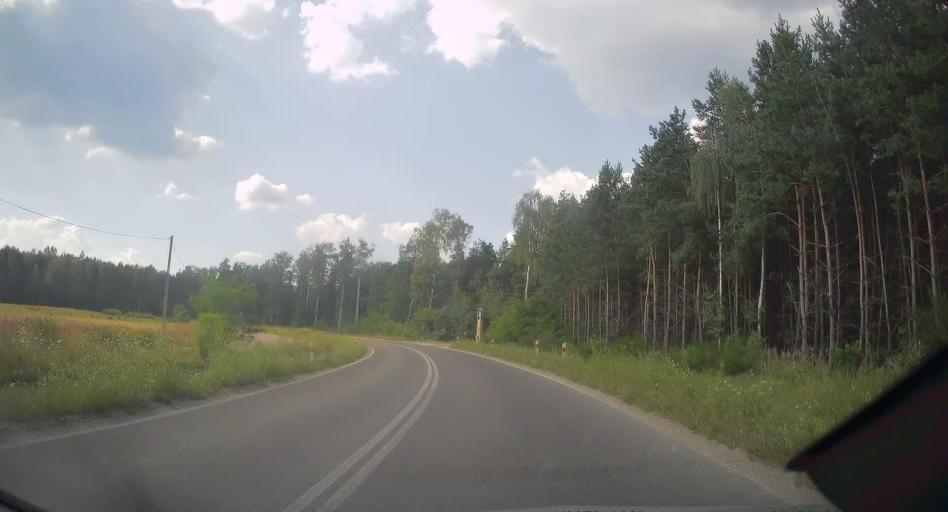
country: PL
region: Swietokrzyskie
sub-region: Powiat kielecki
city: Lopuszno
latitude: 50.8829
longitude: 20.2683
